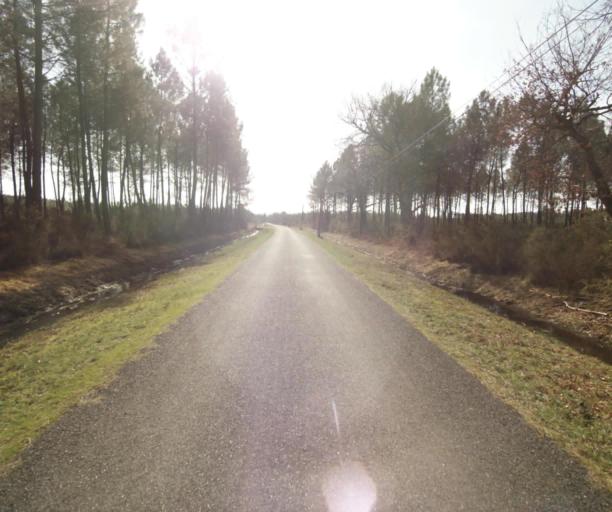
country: FR
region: Aquitaine
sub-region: Departement des Landes
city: Roquefort
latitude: 44.1326
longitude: -0.1889
